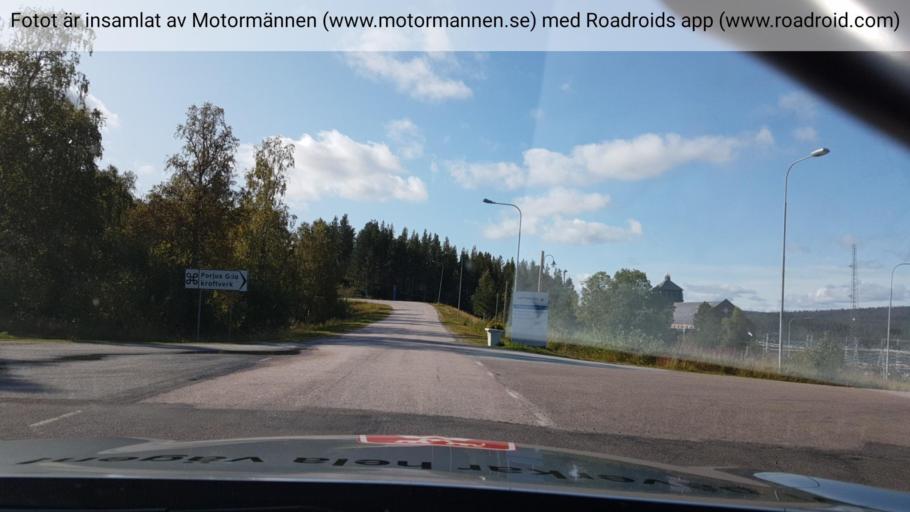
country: SE
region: Norrbotten
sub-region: Jokkmokks Kommun
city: Jokkmokk
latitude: 66.9558
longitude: 19.8021
